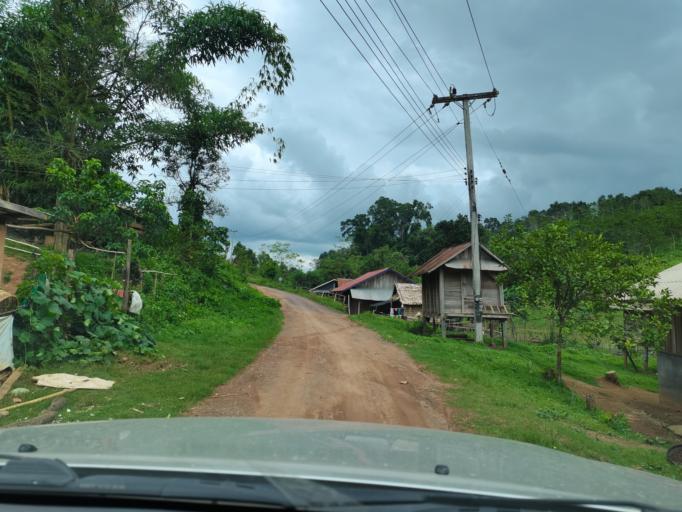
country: LA
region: Loungnamtha
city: Muang Long
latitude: 20.7048
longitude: 101.0107
